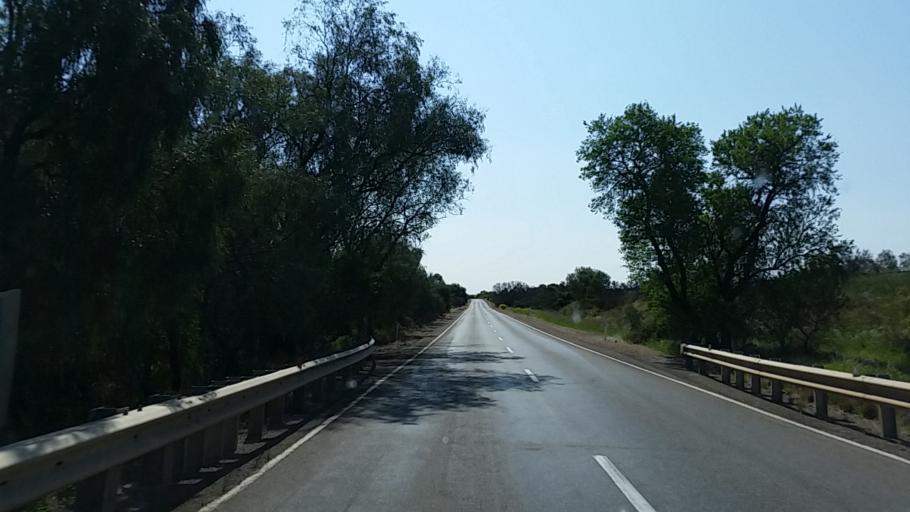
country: AU
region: South Australia
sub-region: Port Pirie City and Dists
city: Crystal Brook
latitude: -33.2383
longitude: 138.3850
